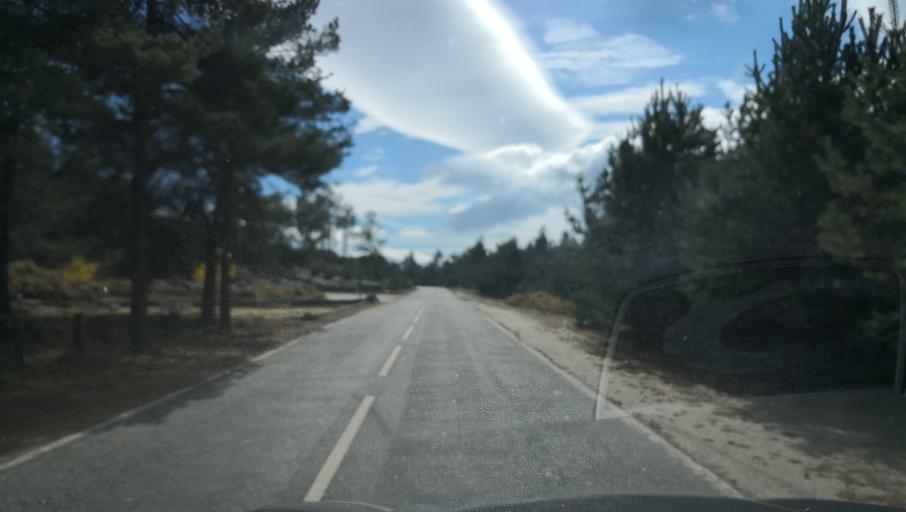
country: PT
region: Vila Real
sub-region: Vila Real
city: Vila Real
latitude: 41.3536
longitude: -7.7923
